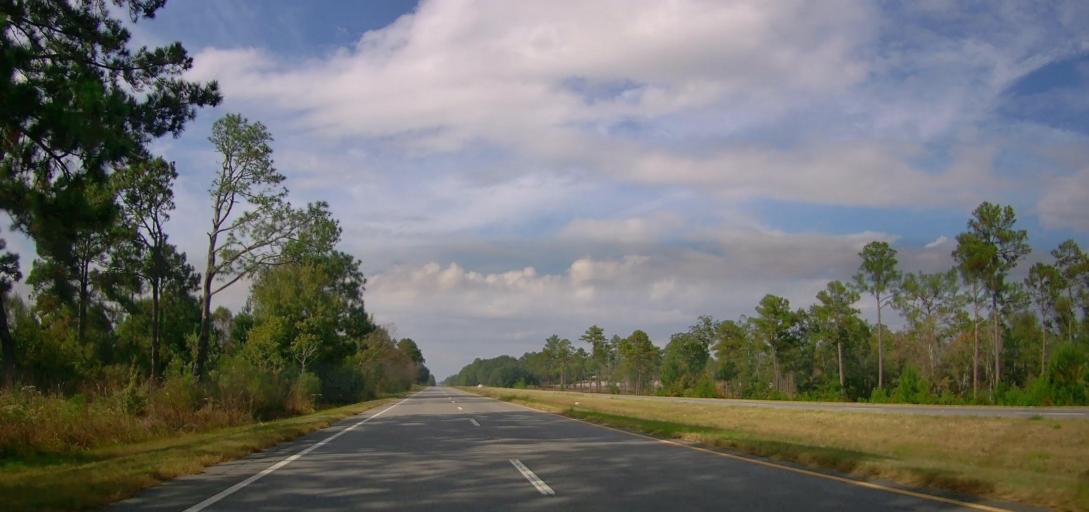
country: US
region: Georgia
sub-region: Thomas County
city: Meigs
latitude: 30.9594
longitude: -84.0289
